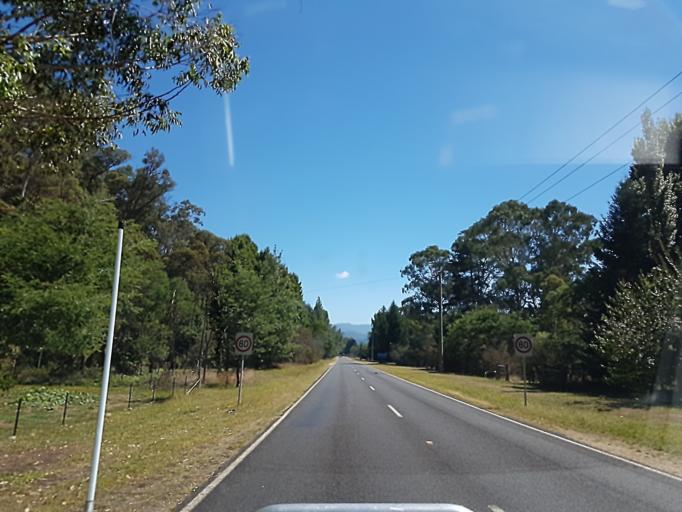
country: AU
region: Victoria
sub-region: Alpine
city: Mount Beauty
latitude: -36.7767
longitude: 147.0322
